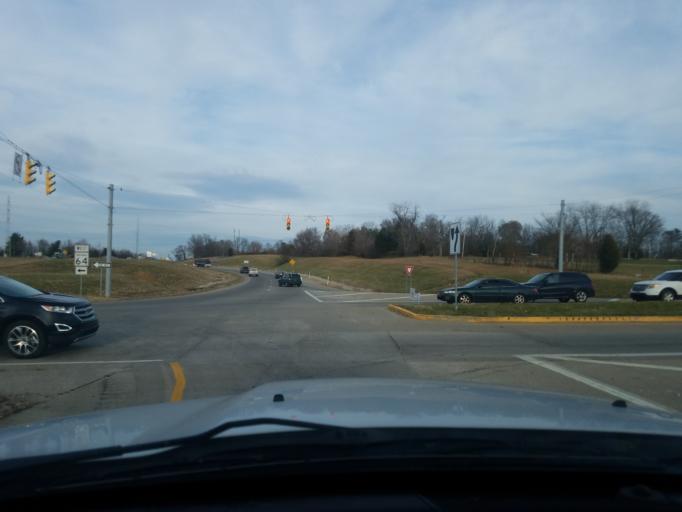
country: US
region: Indiana
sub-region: Floyd County
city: Georgetown
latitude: 38.2866
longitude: -85.9114
